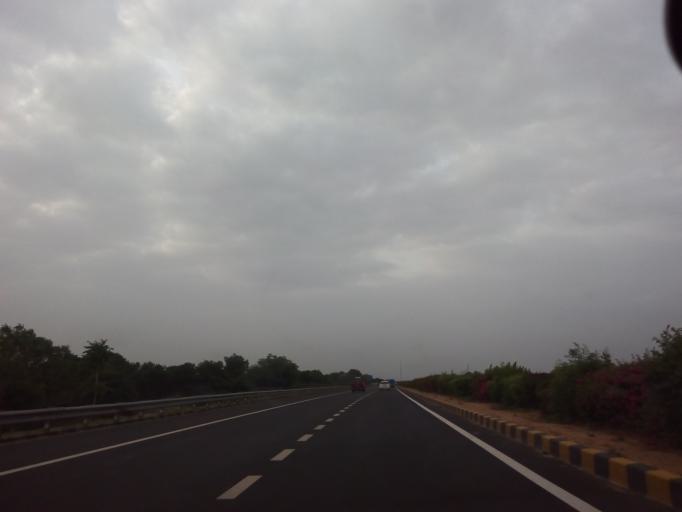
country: IN
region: Gujarat
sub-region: Kheda
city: Mahemdavad
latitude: 22.9165
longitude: 72.7595
